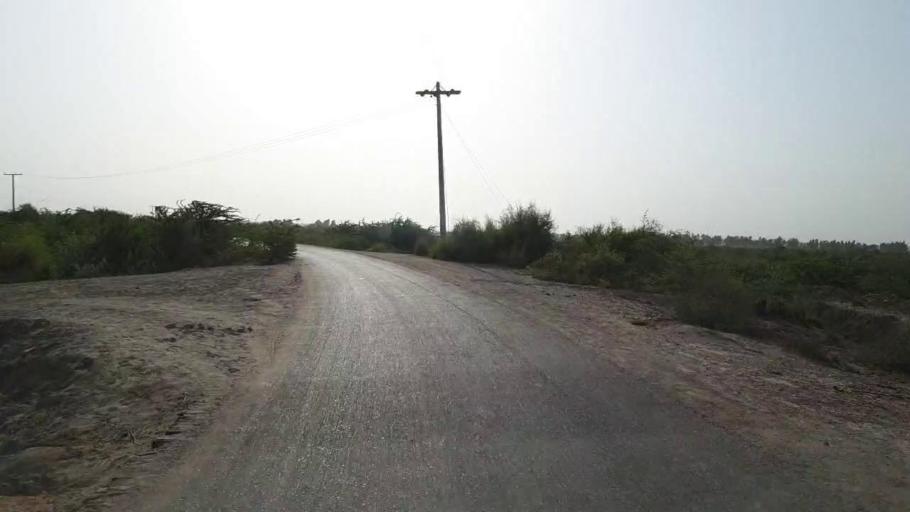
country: PK
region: Sindh
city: Jam Sahib
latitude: 26.4387
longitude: 68.8664
